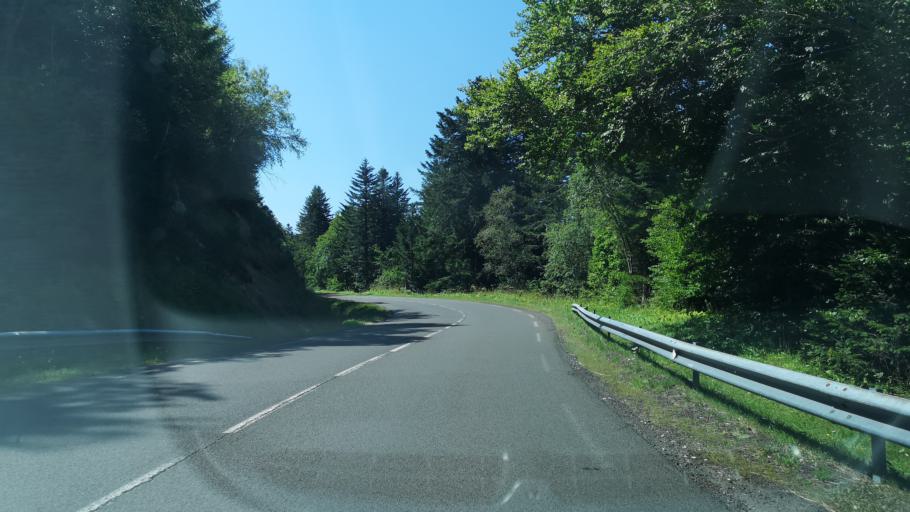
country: FR
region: Auvergne
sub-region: Departement du Puy-de-Dome
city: Mont-Dore
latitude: 45.6000
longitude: 2.8268
